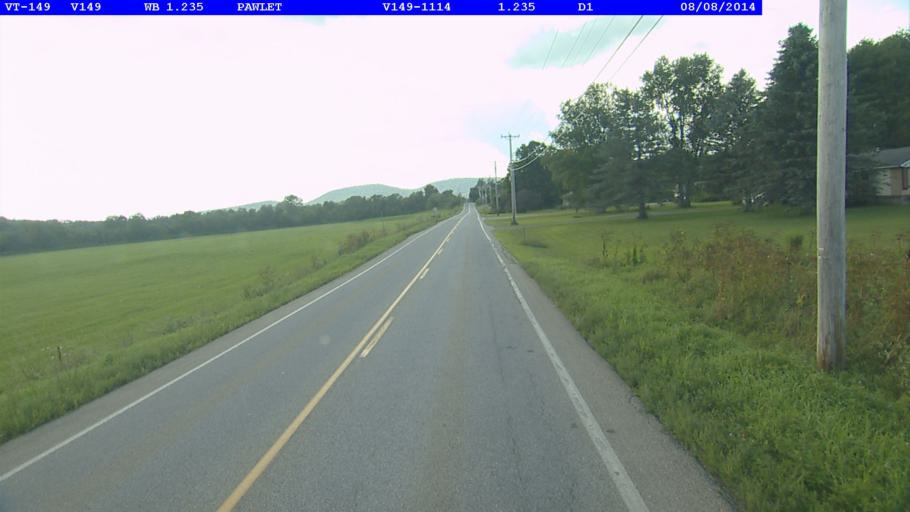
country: US
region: New York
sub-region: Washington County
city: Granville
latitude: 43.4016
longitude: -73.2272
